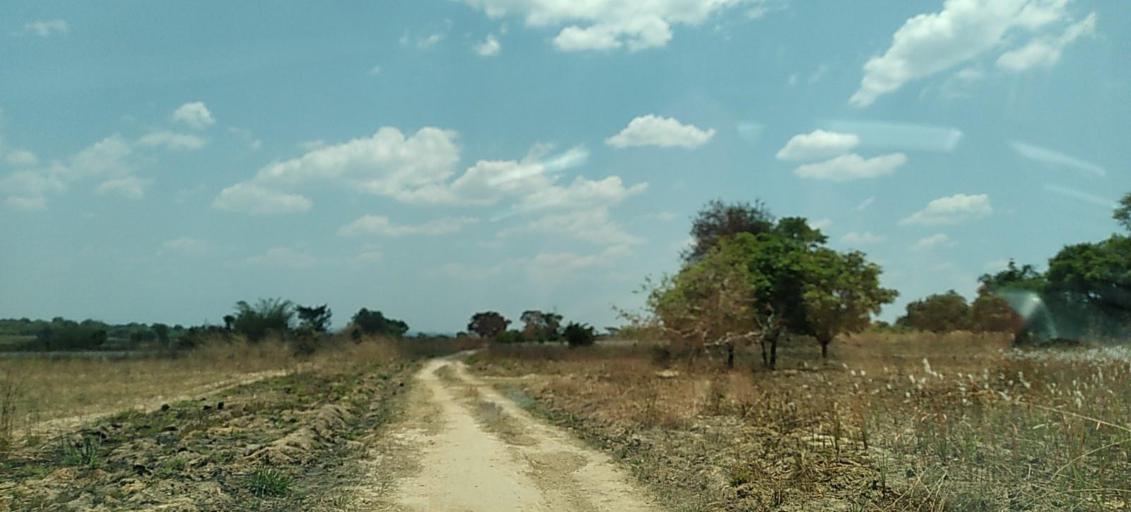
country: ZM
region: Copperbelt
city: Chililabombwe
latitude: -12.4695
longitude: 27.6659
